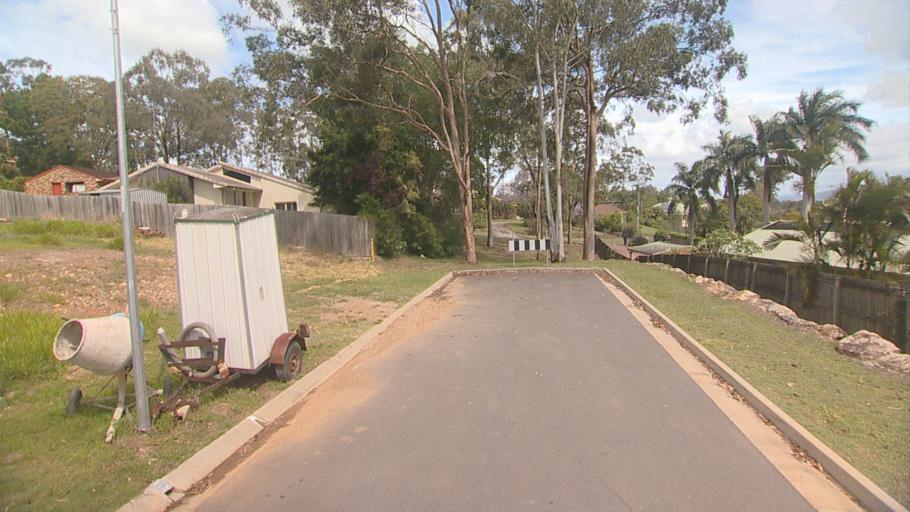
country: AU
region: Queensland
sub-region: Logan
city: Beenleigh
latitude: -27.6679
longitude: 153.1985
